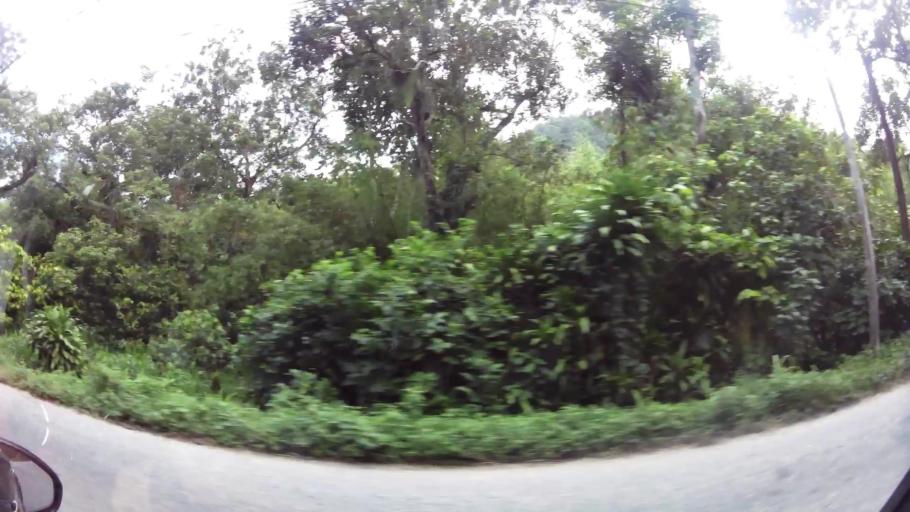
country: TT
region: San Juan/Laventille
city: Laventille
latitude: 10.6884
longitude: -61.4576
